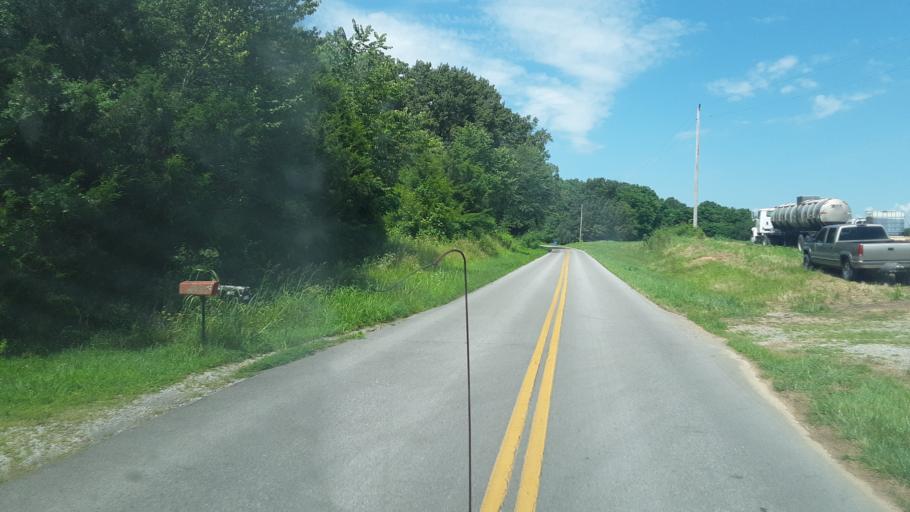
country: US
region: Kentucky
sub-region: Christian County
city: Oak Grove
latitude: 36.7316
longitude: -87.3326
